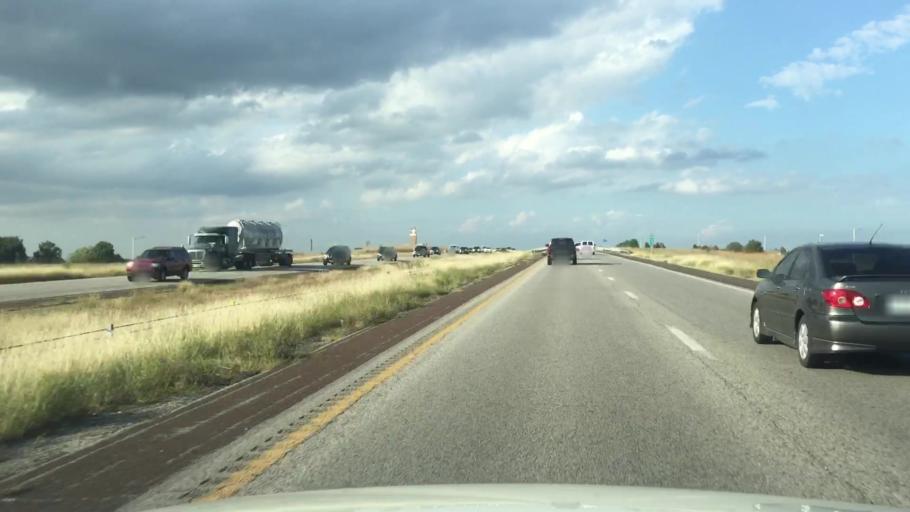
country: US
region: Missouri
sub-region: Jackson County
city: Blue Springs
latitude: 39.0022
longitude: -94.3568
